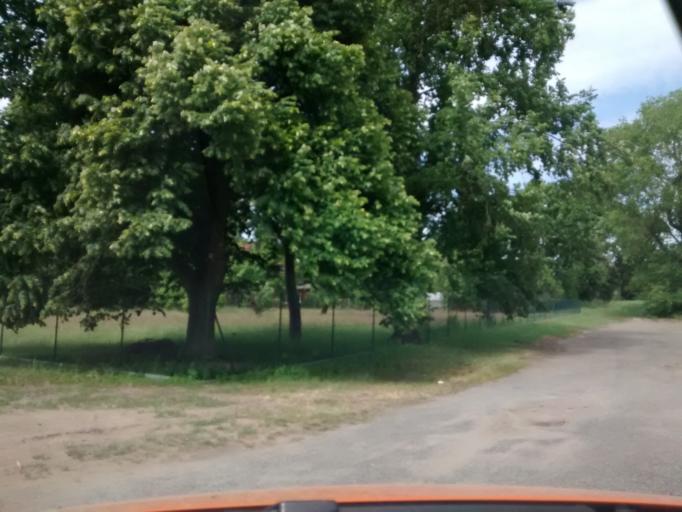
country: DE
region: Brandenburg
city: Ihlow
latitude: 51.8807
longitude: 13.3488
